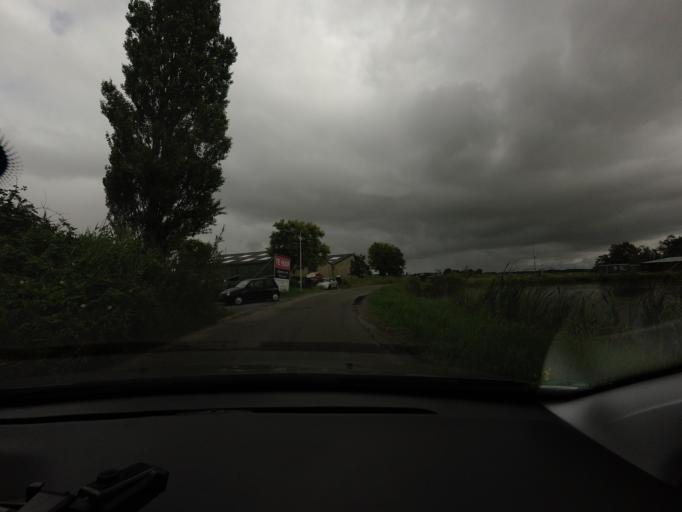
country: NL
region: North Holland
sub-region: Gemeente Haarlem
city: Haarlem
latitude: 52.3925
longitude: 4.6770
